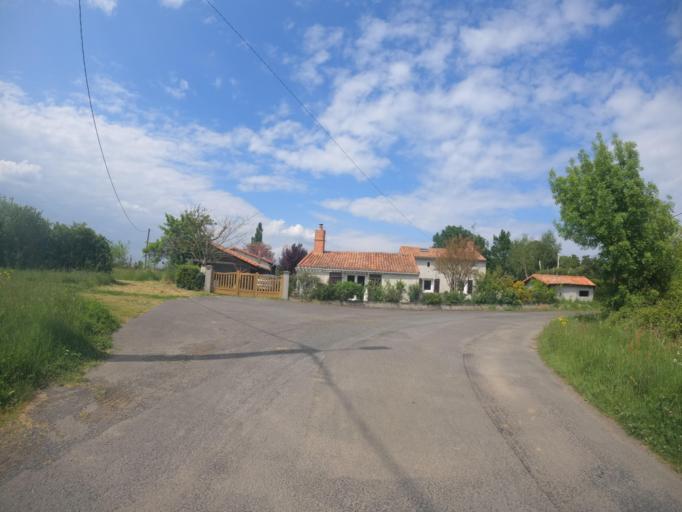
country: FR
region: Poitou-Charentes
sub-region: Departement des Deux-Sevres
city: Saint-Varent
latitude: 46.8940
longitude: -0.2899
